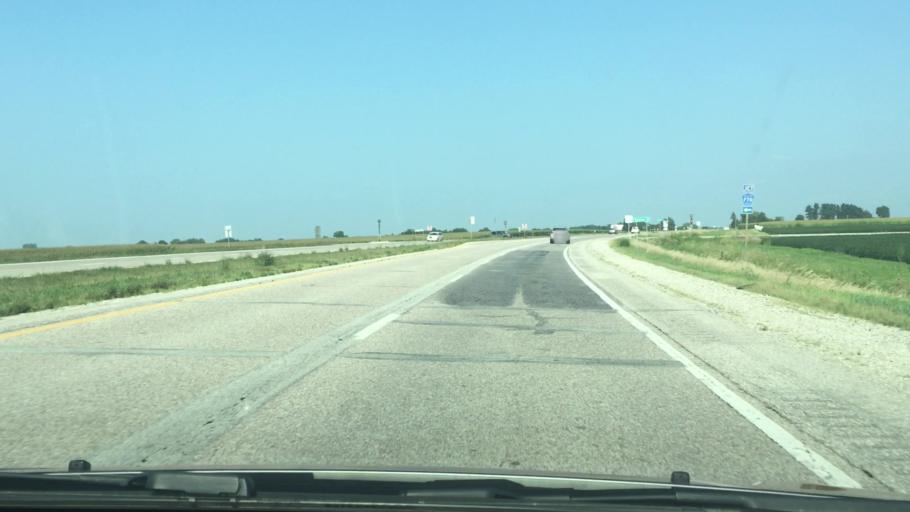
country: US
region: Iowa
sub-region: Muscatine County
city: Wilton
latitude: 41.4977
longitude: -90.9703
